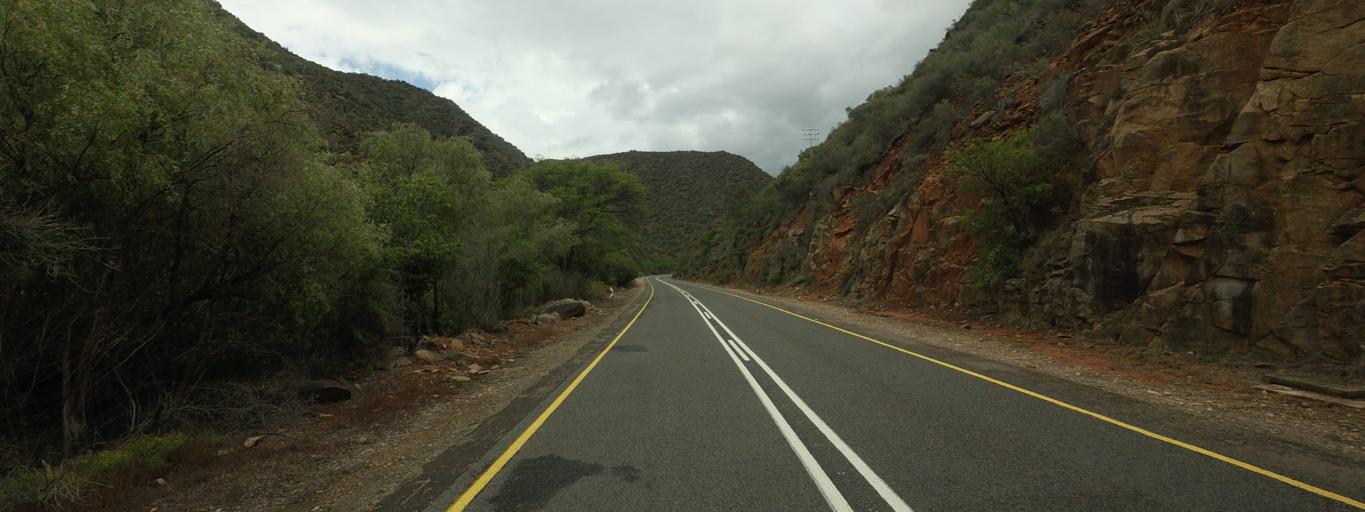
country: ZA
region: Western Cape
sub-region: Eden District Municipality
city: Oudtshoorn
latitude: -33.4483
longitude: 22.2521
